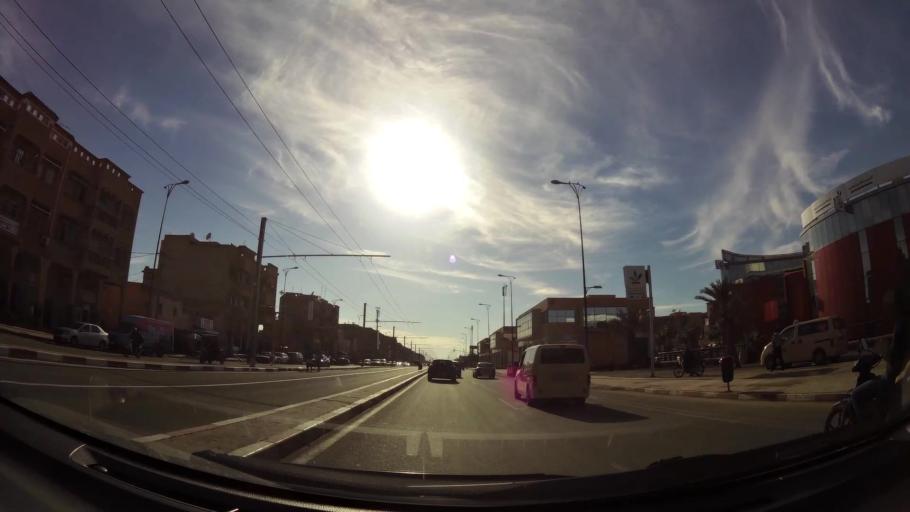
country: MA
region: Marrakech-Tensift-Al Haouz
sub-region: Marrakech
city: Marrakesh
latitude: 31.6280
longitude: -8.0607
